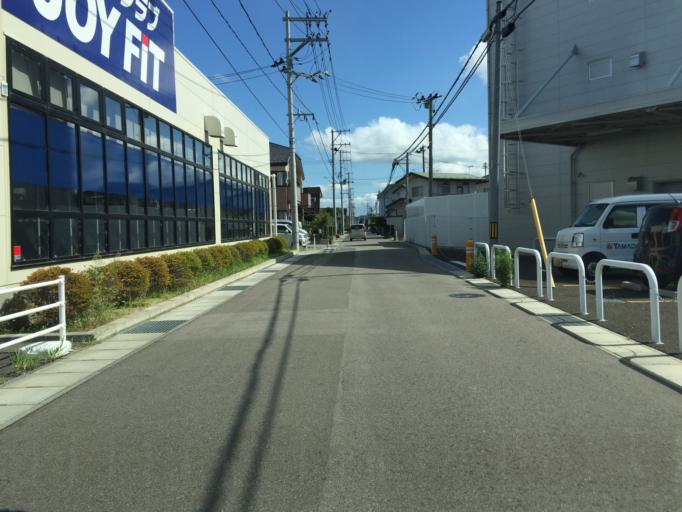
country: JP
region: Fukushima
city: Fukushima-shi
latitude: 37.7299
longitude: 140.4511
